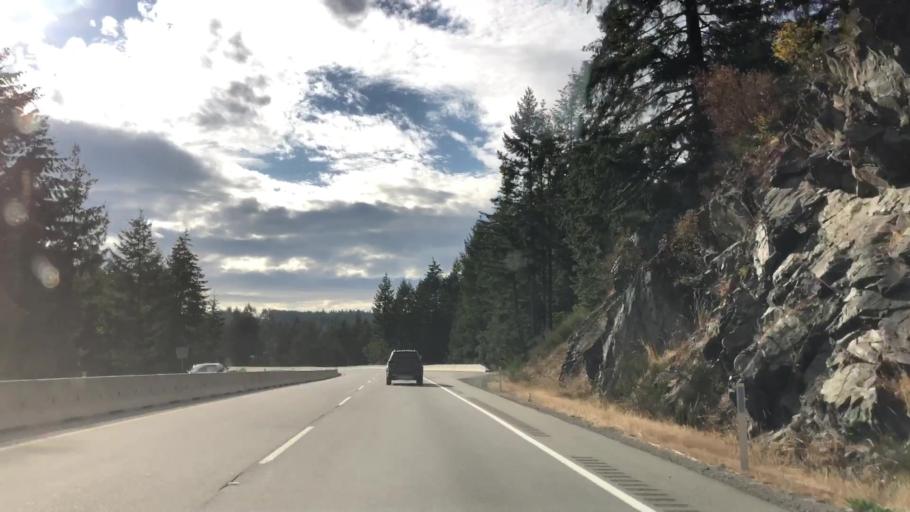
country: CA
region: British Columbia
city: Langford
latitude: 48.5680
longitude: -123.5499
